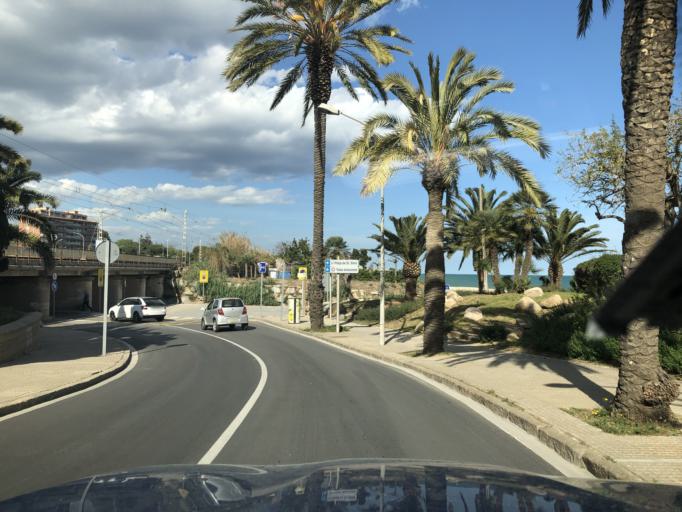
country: ES
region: Catalonia
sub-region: Provincia de Barcelona
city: Mataro
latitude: 41.5405
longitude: 2.4565
